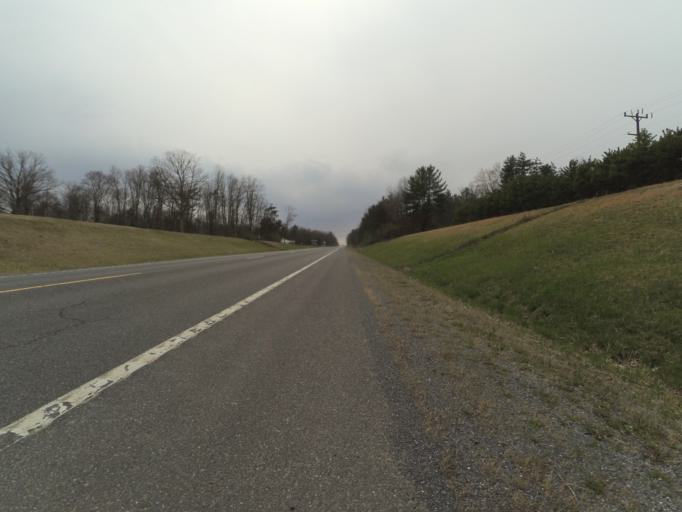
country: US
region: Pennsylvania
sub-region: Centre County
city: Zion
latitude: 40.9884
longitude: -77.7170
